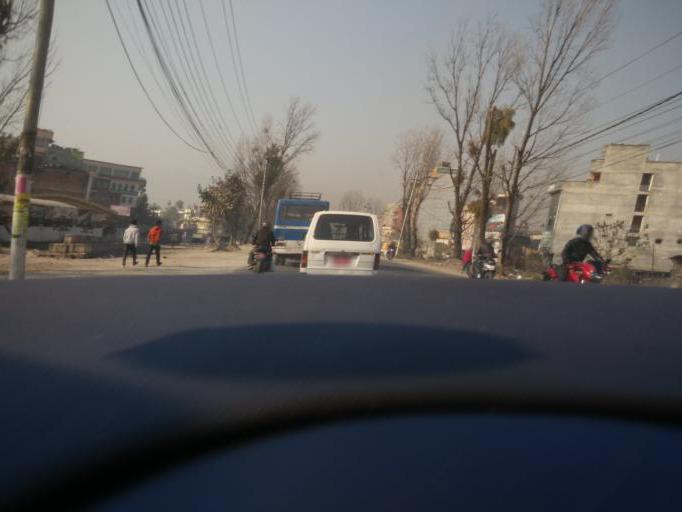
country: NP
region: Central Region
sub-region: Bagmati Zone
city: Kathmandu
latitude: 27.7379
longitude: 85.3248
